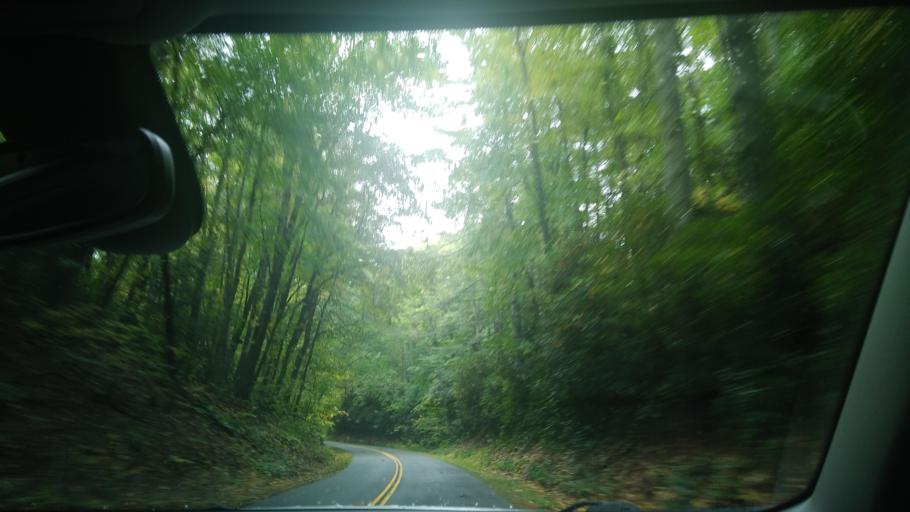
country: US
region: North Carolina
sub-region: Mitchell County
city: Spruce Pine
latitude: 35.8770
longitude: -82.0000
